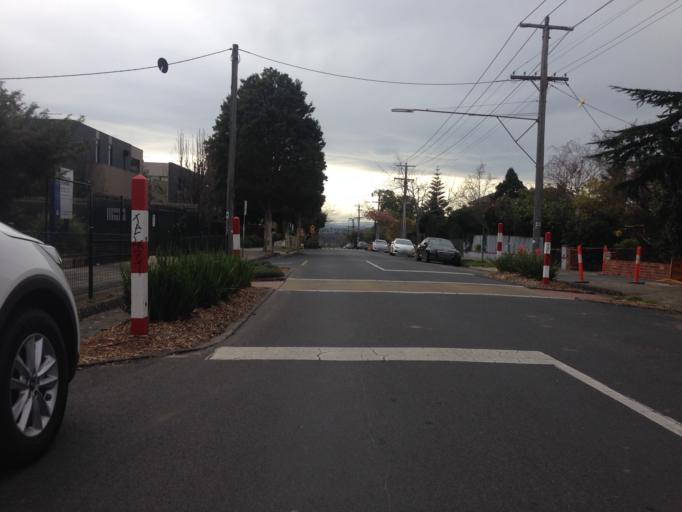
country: AU
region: Victoria
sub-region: Boroondara
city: Kew
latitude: -37.8039
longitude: 145.0345
